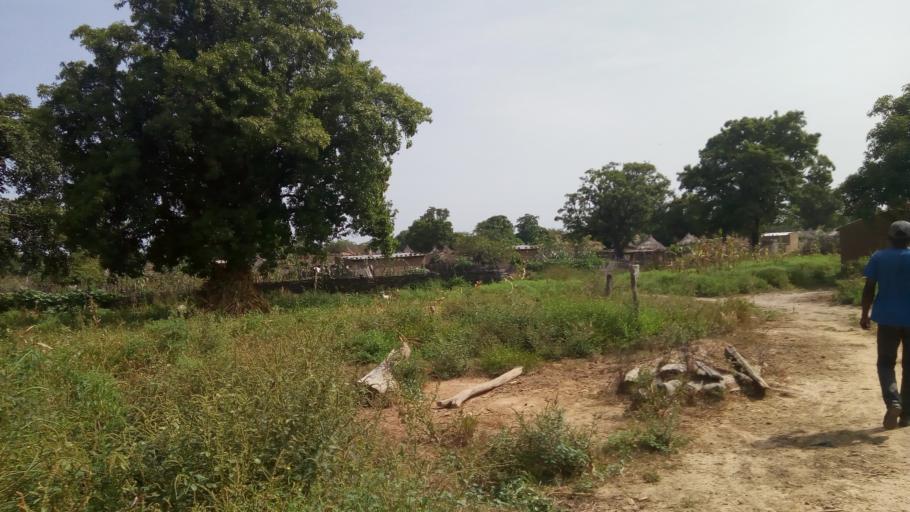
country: ML
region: Kayes
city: Kita
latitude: 13.1689
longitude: -8.7636
